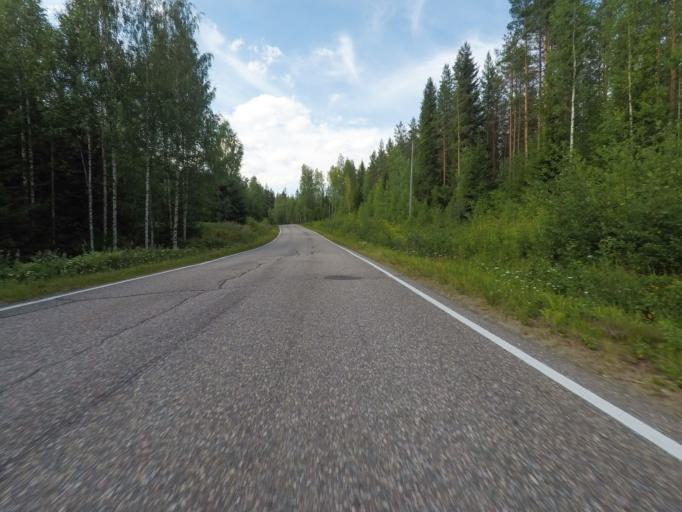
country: FI
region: Southern Savonia
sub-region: Savonlinna
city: Sulkava
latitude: 61.7329
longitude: 28.2098
